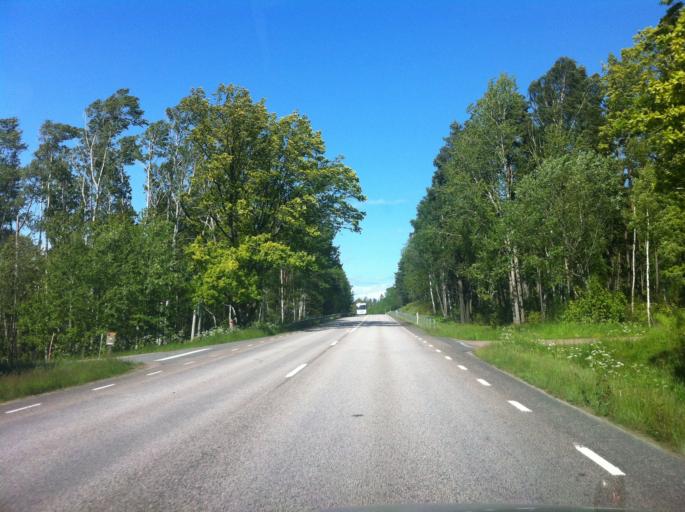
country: SE
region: Vaestra Goetaland
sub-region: Gullspangs Kommun
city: Gullspang
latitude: 59.0371
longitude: 14.1329
